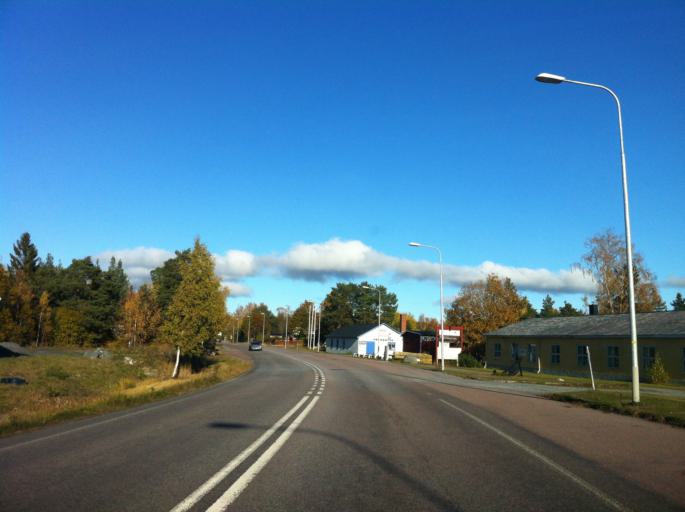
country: SE
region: Uppsala
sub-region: Osthammars Kommun
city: Oregrund
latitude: 60.3277
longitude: 18.4257
